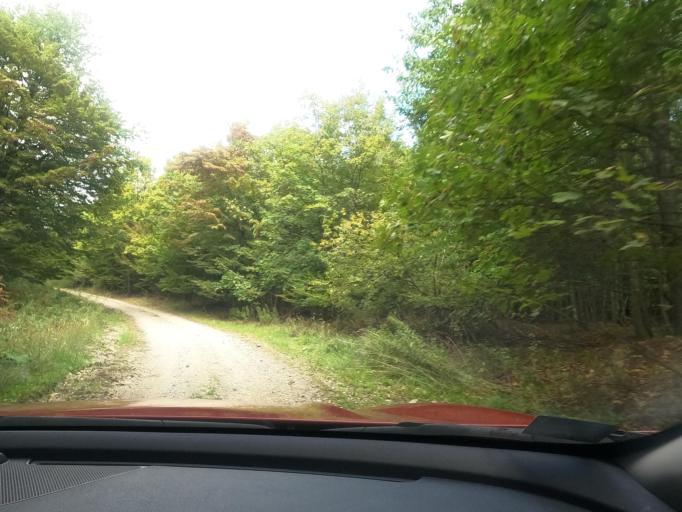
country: BA
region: Federation of Bosnia and Herzegovina
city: Velika Kladusa
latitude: 45.2593
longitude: 15.7883
